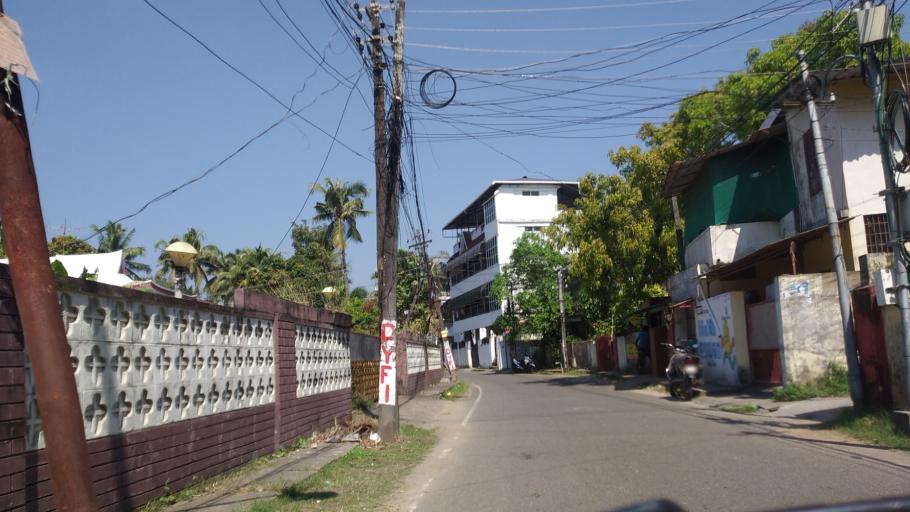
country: IN
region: Kerala
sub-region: Ernakulam
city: Cochin
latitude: 9.9410
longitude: 76.2483
